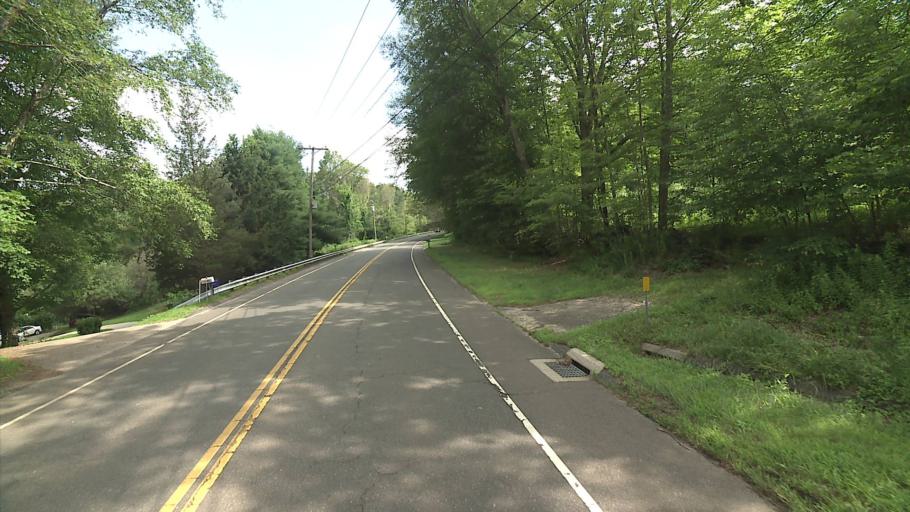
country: US
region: Connecticut
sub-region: Middlesex County
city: Clinton
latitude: 41.3202
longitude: -72.4942
